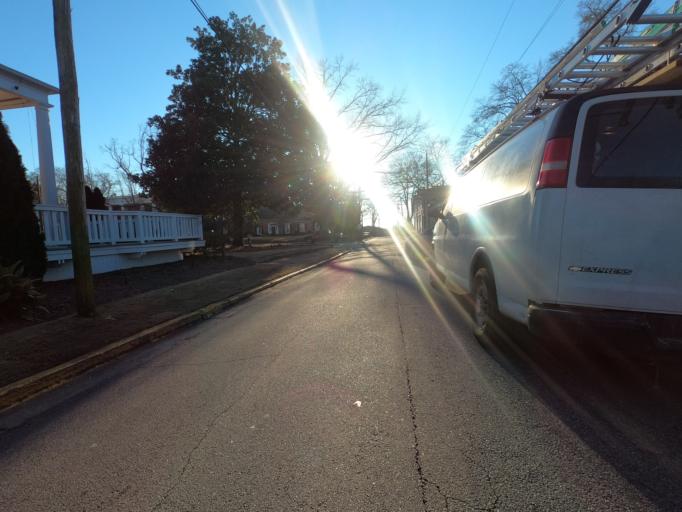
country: US
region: Georgia
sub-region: Clarke County
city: Athens
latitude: 33.9528
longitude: -83.3871
